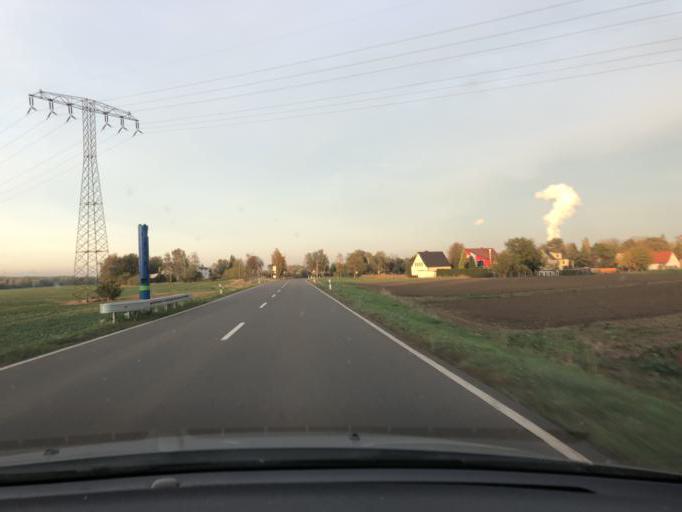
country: DE
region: Saxony
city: Elstertrebnitz
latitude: 51.1326
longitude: 12.2208
